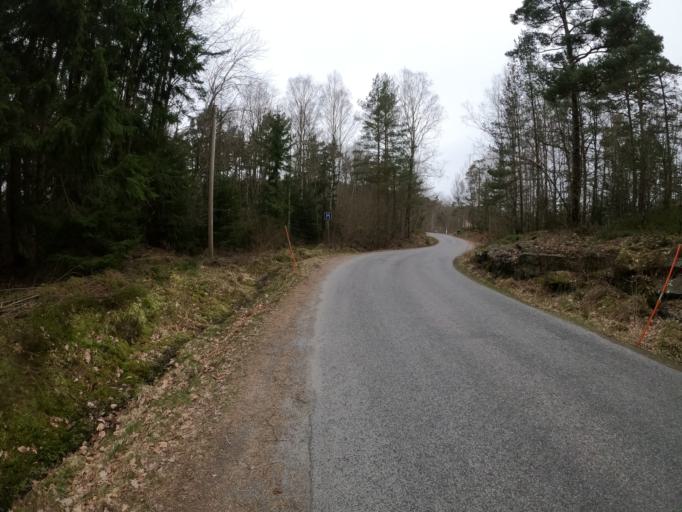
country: SE
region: Vaestra Goetaland
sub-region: Harryda Kommun
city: Molnlycke
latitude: 57.6409
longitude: 12.1070
